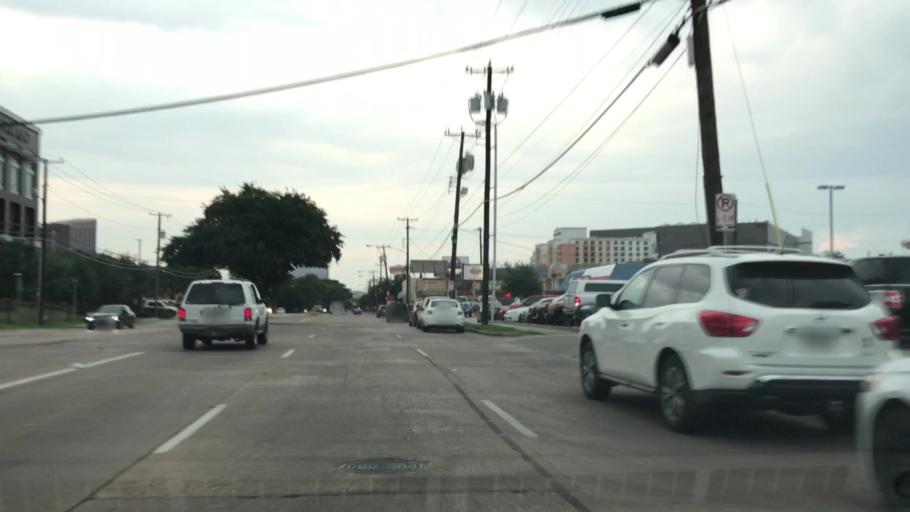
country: US
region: Texas
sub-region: Dallas County
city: Dallas
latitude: 32.7967
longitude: -96.8242
